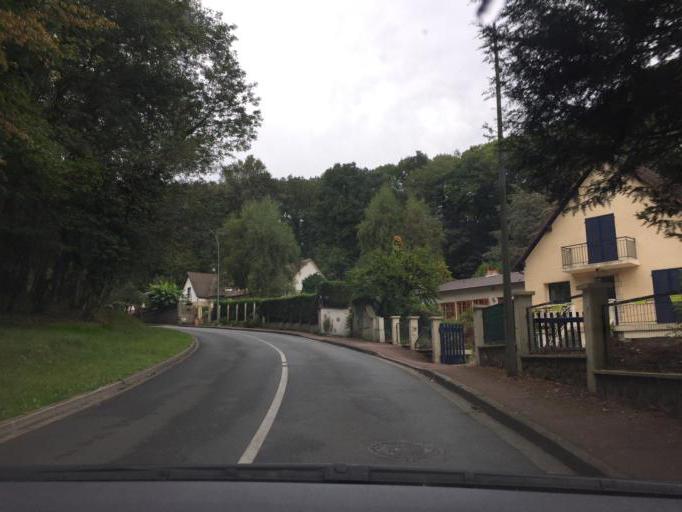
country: FR
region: Ile-de-France
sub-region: Departement de l'Essonne
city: Villiers-le-Bacle
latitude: 48.7249
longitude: 2.1232
